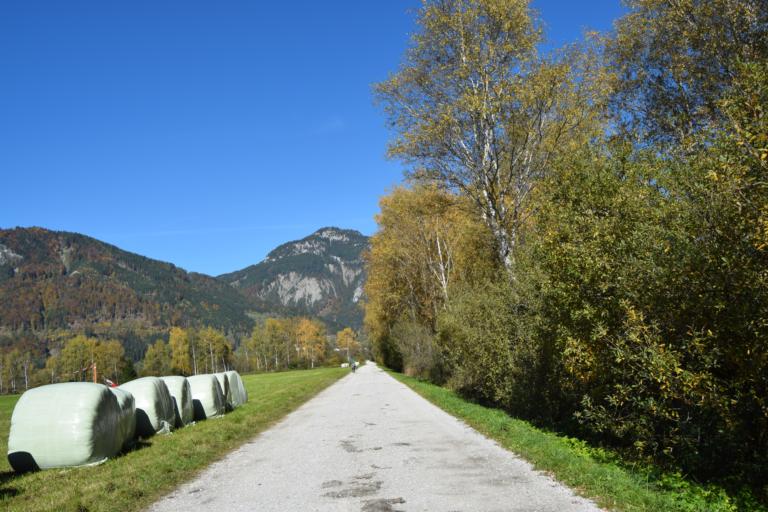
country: AT
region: Styria
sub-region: Politischer Bezirk Liezen
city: Irdning
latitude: 47.5183
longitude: 14.1051
